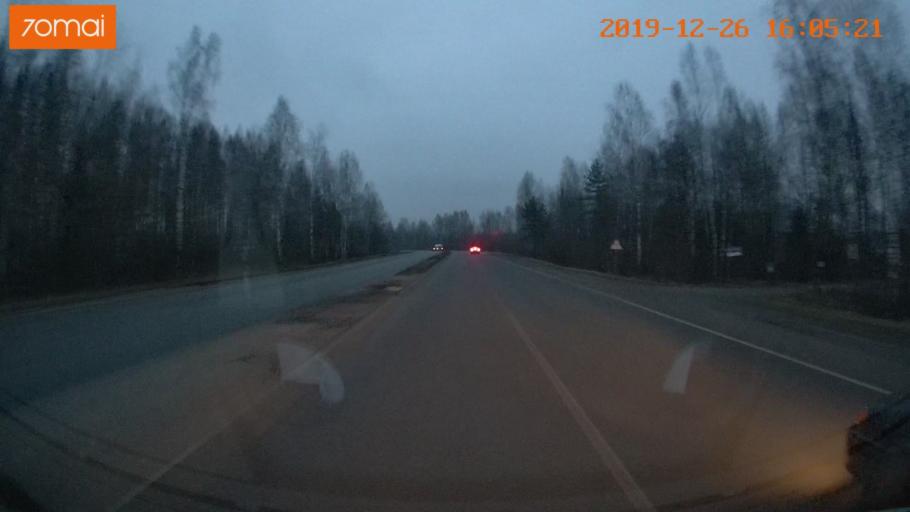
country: RU
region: Jaroslavl
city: Rybinsk
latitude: 58.0060
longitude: 38.8934
